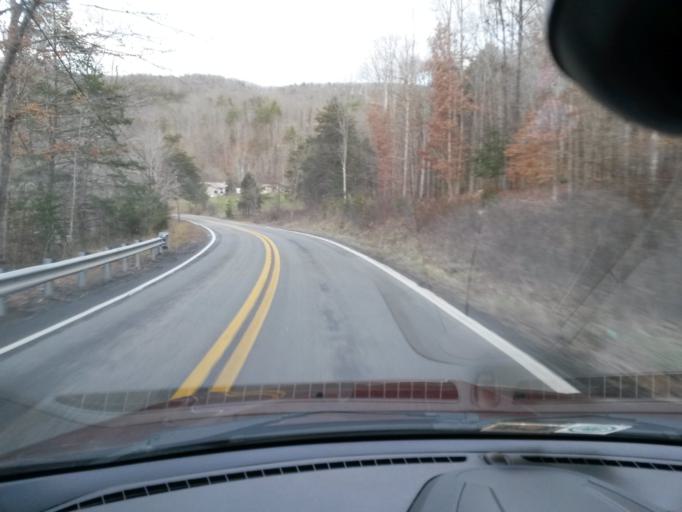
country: US
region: West Virginia
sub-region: Monroe County
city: Union
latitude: 37.5067
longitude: -80.6096
